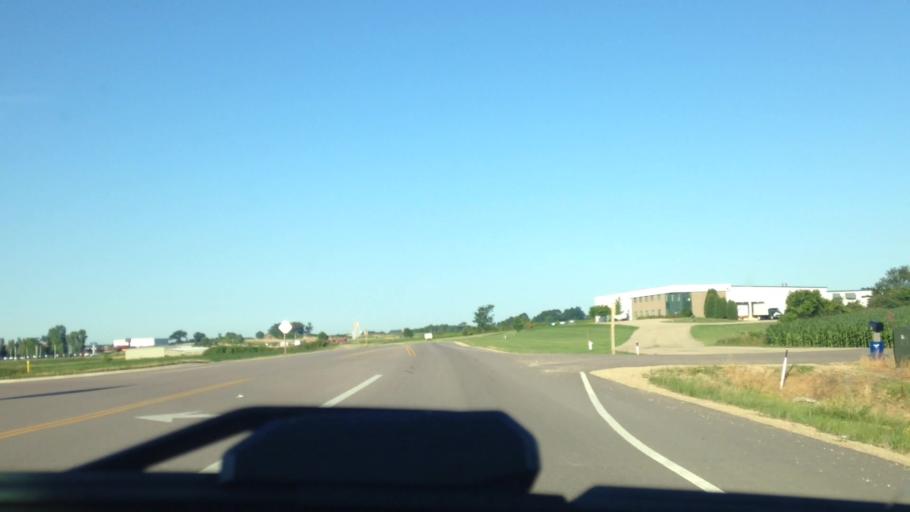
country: US
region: Wisconsin
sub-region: Columbia County
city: Columbus
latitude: 43.3495
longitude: -89.0401
